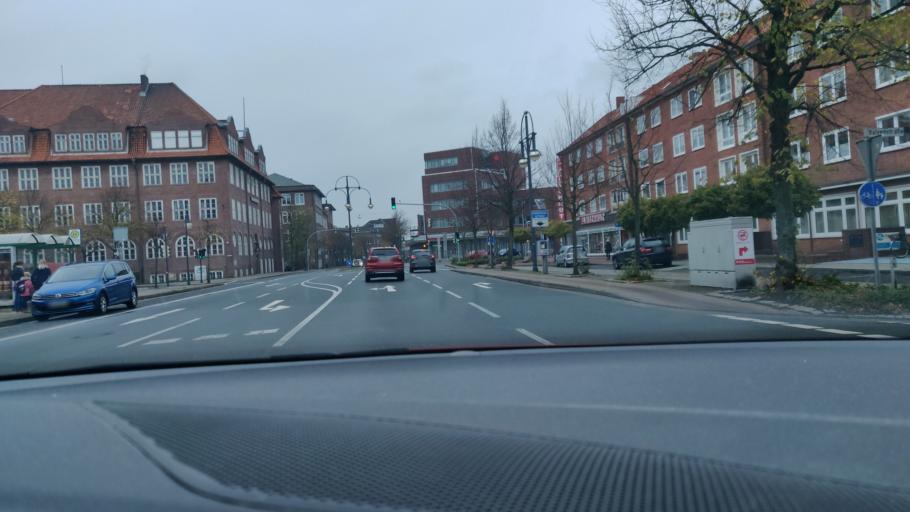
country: DE
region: Lower Saxony
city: Cuxhaven
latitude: 53.8609
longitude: 8.6950
